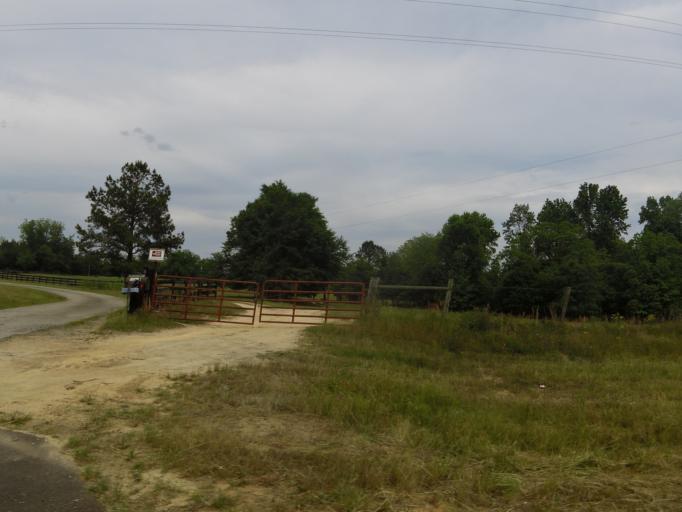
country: US
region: Georgia
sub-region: McDuffie County
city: Thomson
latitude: 33.3854
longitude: -82.4726
